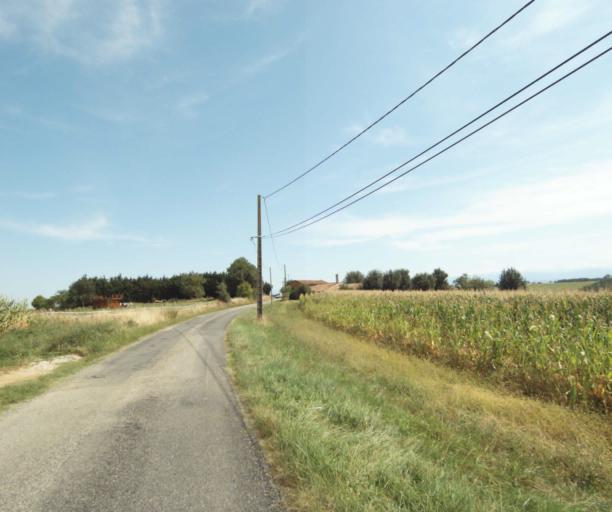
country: FR
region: Midi-Pyrenees
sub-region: Departement de la Haute-Garonne
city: Gaillac-Toulza
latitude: 43.2619
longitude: 1.4161
